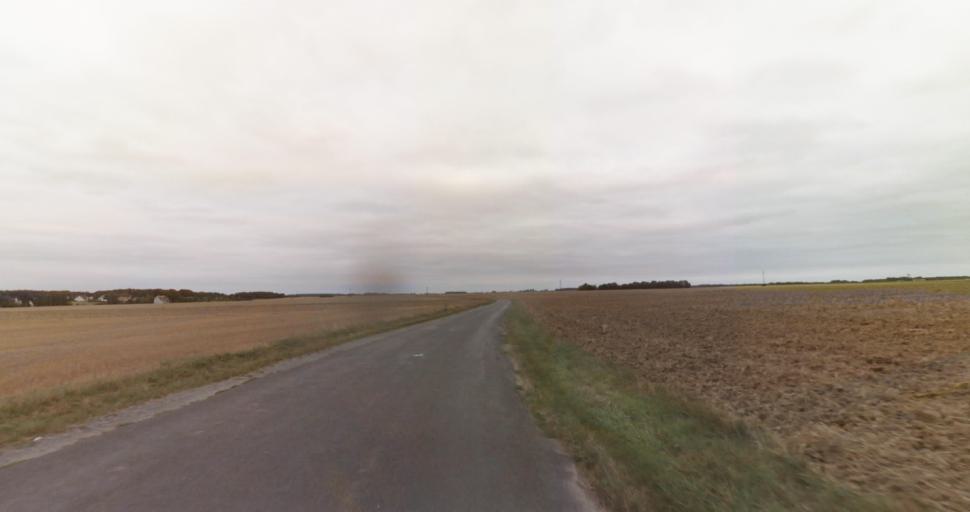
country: FR
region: Haute-Normandie
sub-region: Departement de l'Eure
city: Saint-Germain-sur-Avre
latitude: 48.7970
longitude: 1.2792
